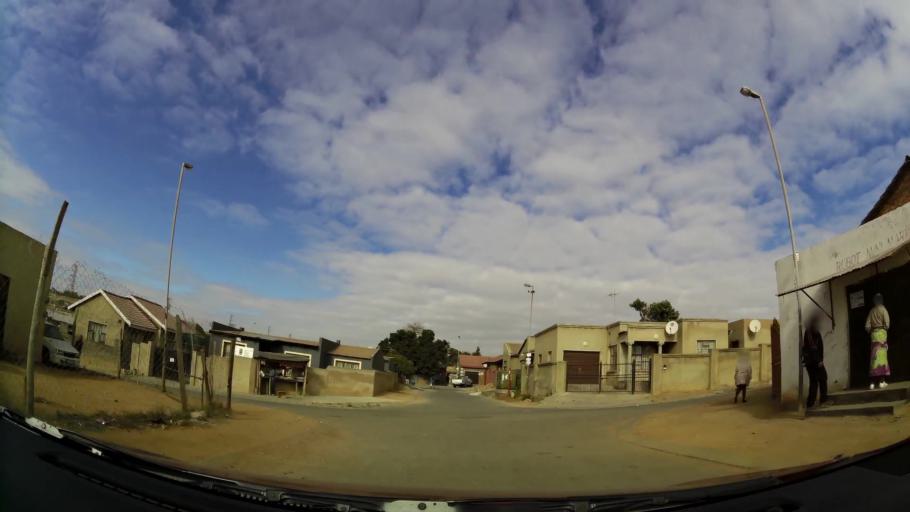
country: ZA
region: Gauteng
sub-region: City of Johannesburg Metropolitan Municipality
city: Modderfontein
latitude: -26.0531
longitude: 28.1821
